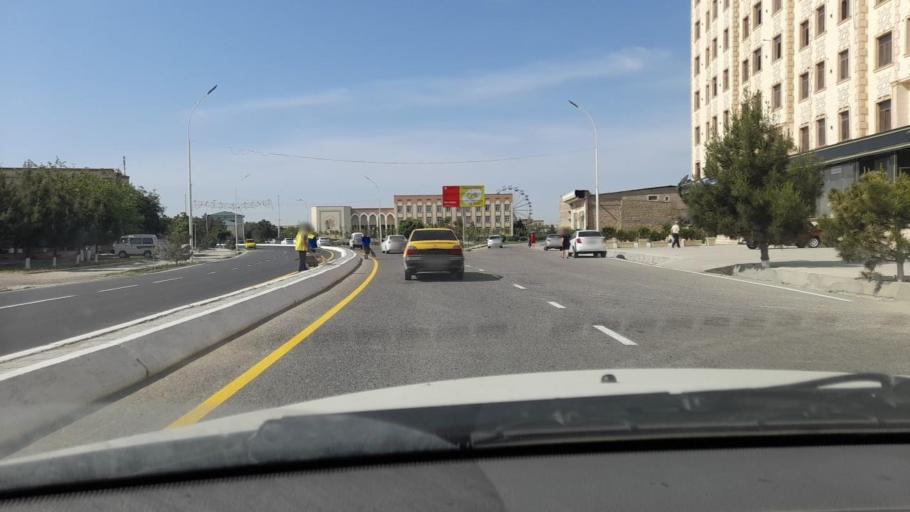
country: UZ
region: Bukhara
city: Bukhara
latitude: 39.7860
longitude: 64.4298
